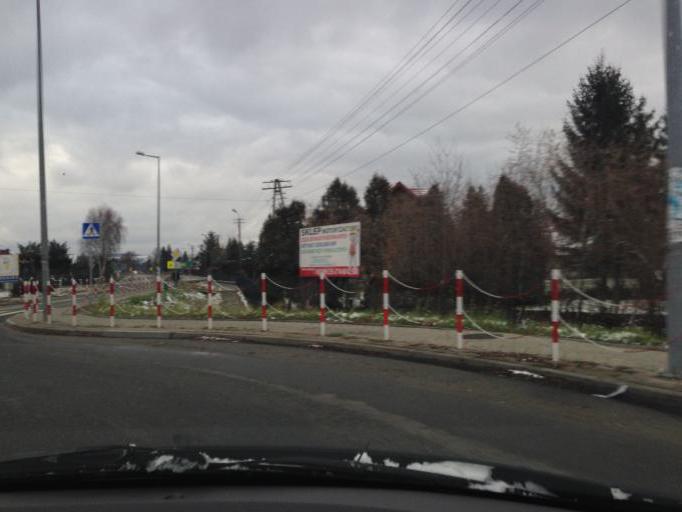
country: PL
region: Lesser Poland Voivodeship
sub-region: Powiat brzeski
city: Czchow
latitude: 49.8511
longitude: 20.6888
